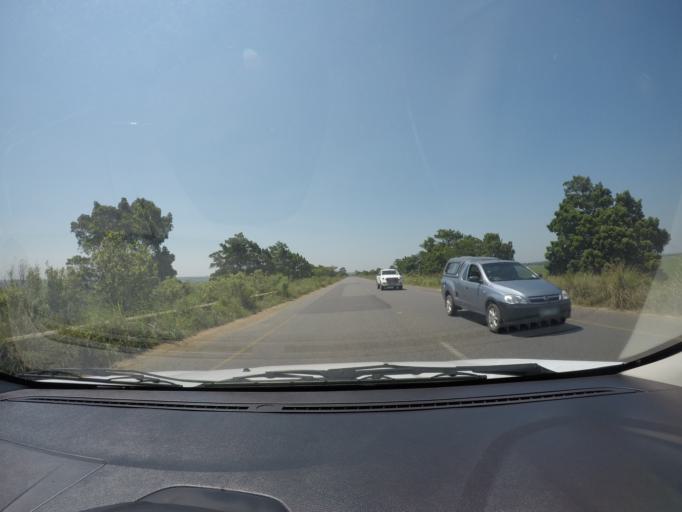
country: ZA
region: KwaZulu-Natal
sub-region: uThungulu District Municipality
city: Empangeni
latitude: -28.7966
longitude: 31.9583
